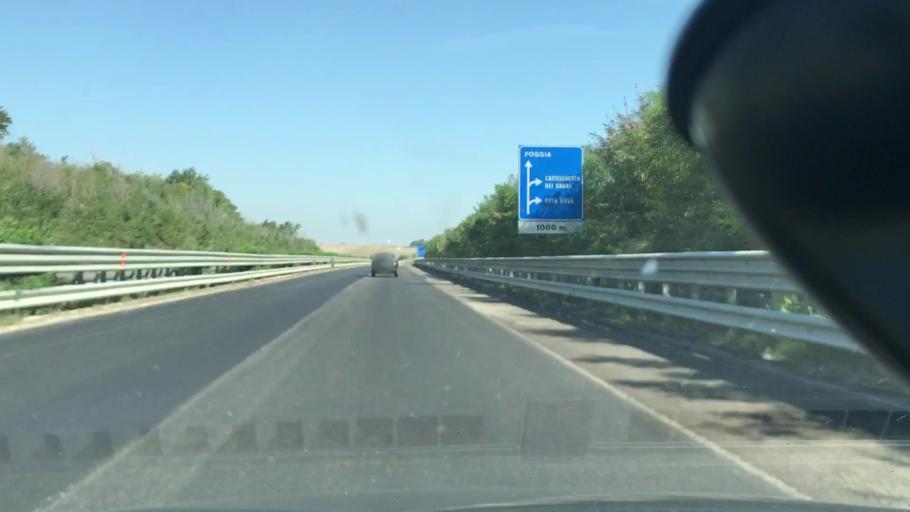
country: IT
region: Apulia
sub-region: Provincia di Foggia
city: Ordona
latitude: 41.2946
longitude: 15.5541
